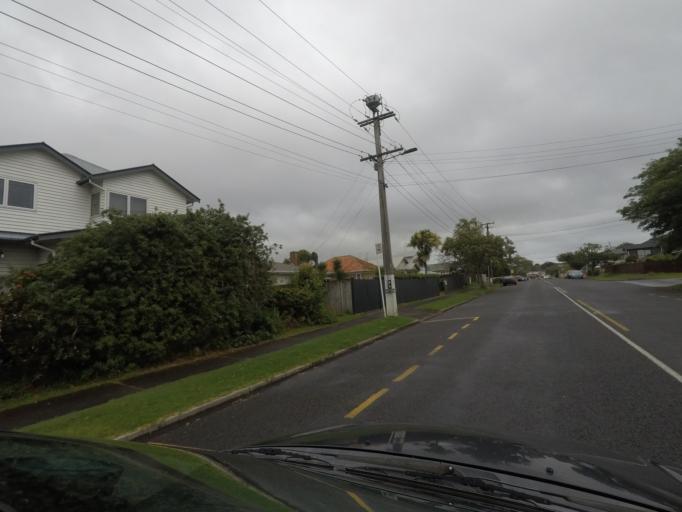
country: NZ
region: Auckland
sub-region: Auckland
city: Auckland
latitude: -36.8874
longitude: 174.7328
